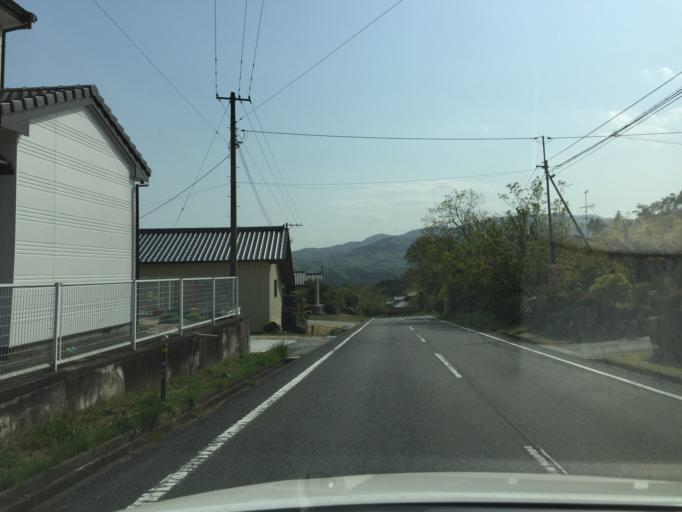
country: JP
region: Fukushima
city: Iwaki
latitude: 37.1514
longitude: 140.8595
